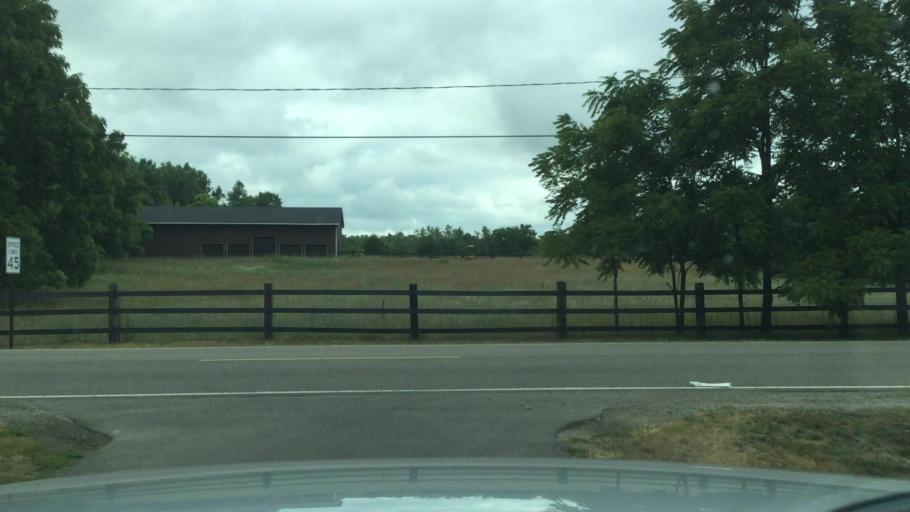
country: US
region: Michigan
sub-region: Genesee County
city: Beecher
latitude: 43.0911
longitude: -83.6265
